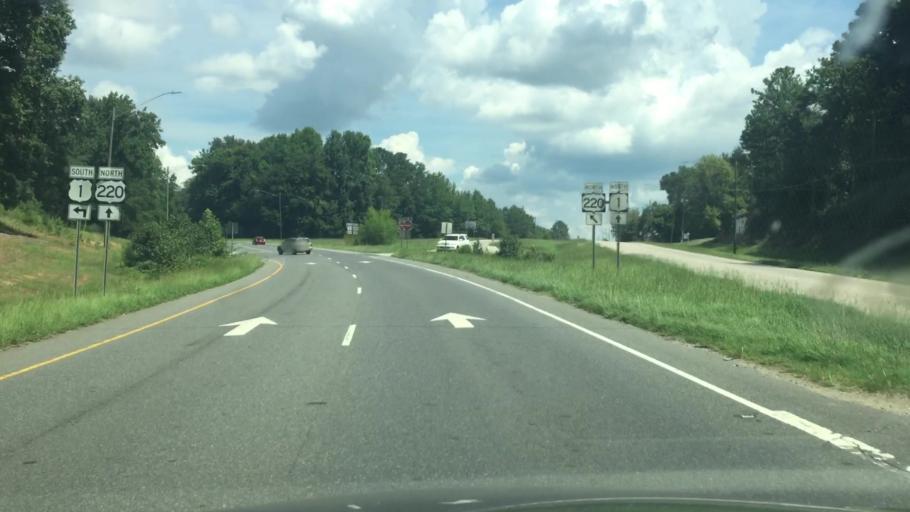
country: US
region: North Carolina
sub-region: Richmond County
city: Rockingham
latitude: 34.9254
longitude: -79.7801
